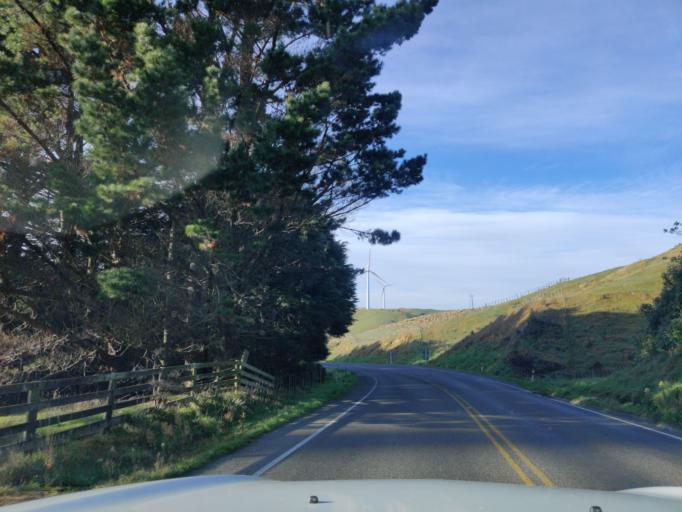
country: NZ
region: Manawatu-Wanganui
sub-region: Palmerston North City
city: Palmerston North
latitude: -40.2967
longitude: 175.8088
